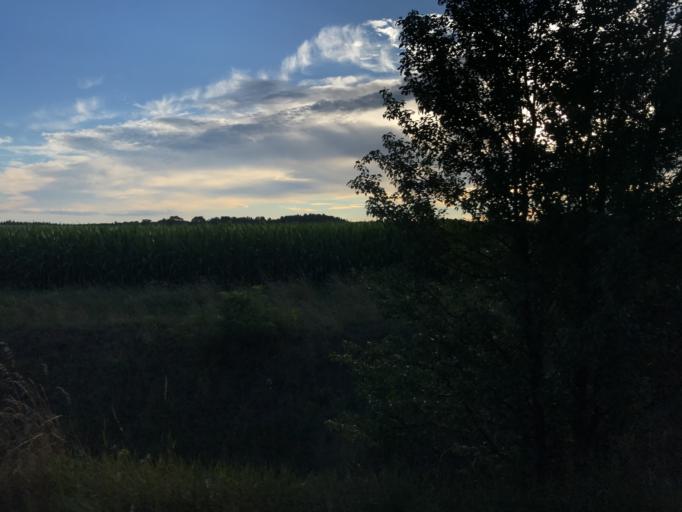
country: CZ
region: Jihocesky
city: Suchdol nad Luznici
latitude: 48.8779
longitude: 14.8785
